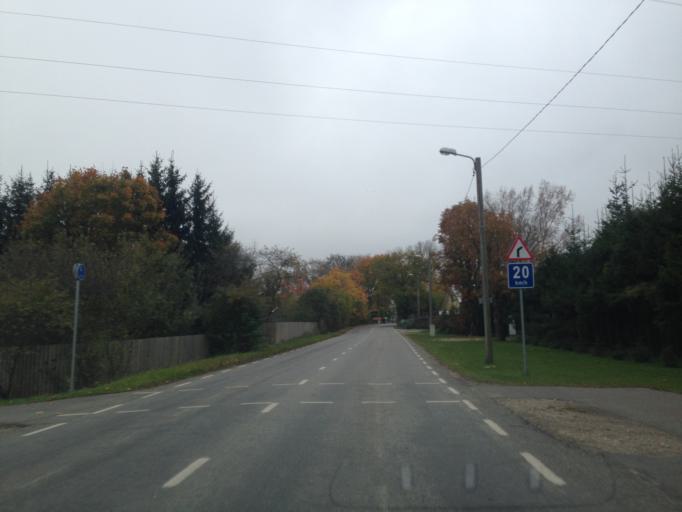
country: EE
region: Harju
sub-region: Saue linn
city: Saue
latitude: 59.3260
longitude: 24.5474
